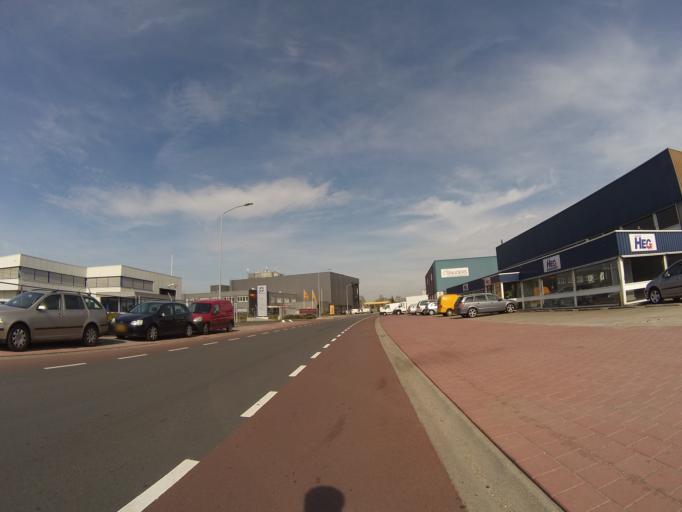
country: NL
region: Gelderland
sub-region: Gemeente Nijkerk
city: Nijkerk
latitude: 52.2337
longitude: 5.4775
